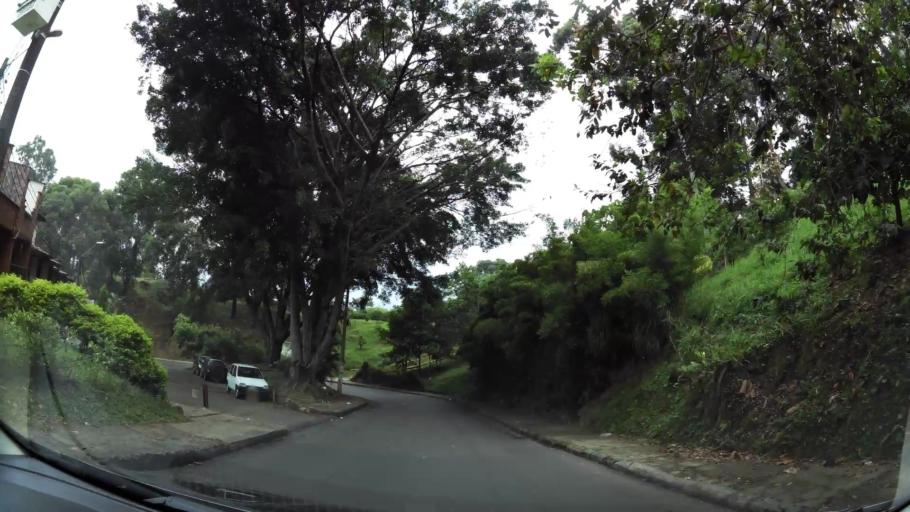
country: CO
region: Antioquia
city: Medellin
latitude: 6.2340
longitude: -75.5620
